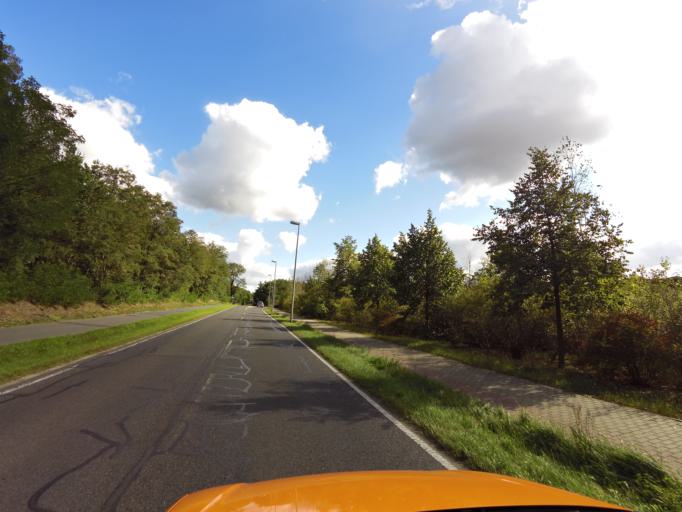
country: DE
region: Brandenburg
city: Luckenwalde
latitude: 52.0972
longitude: 13.1430
